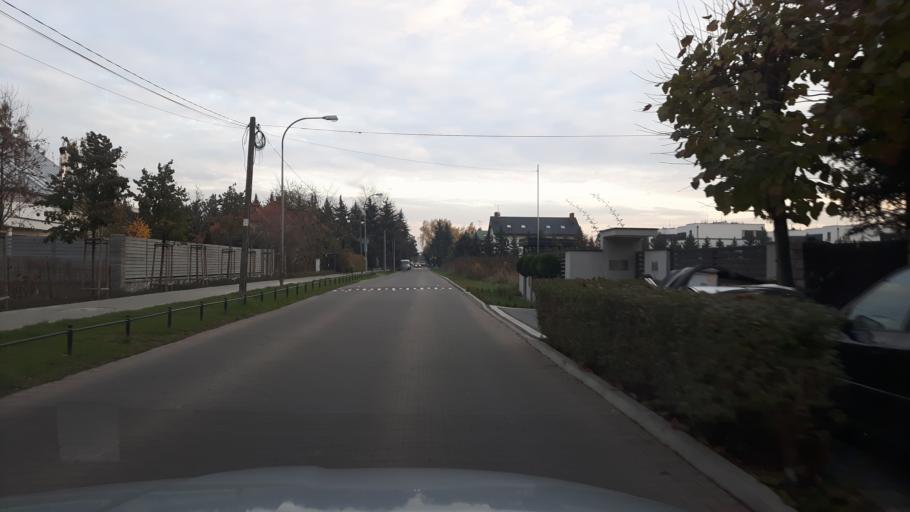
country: PL
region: Masovian Voivodeship
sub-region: Warszawa
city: Wilanow
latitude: 52.1741
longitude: 21.1114
